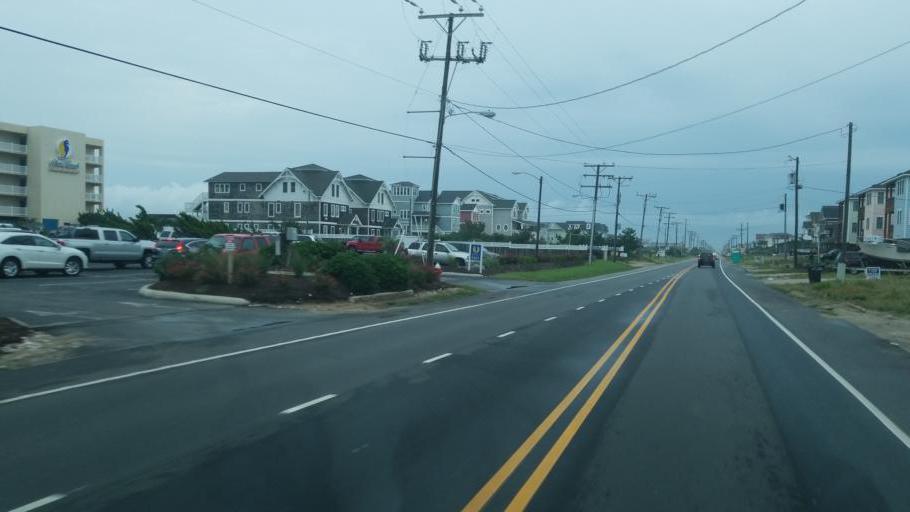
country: US
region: North Carolina
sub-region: Dare County
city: Kill Devil Hills
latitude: 36.0342
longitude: -75.6695
